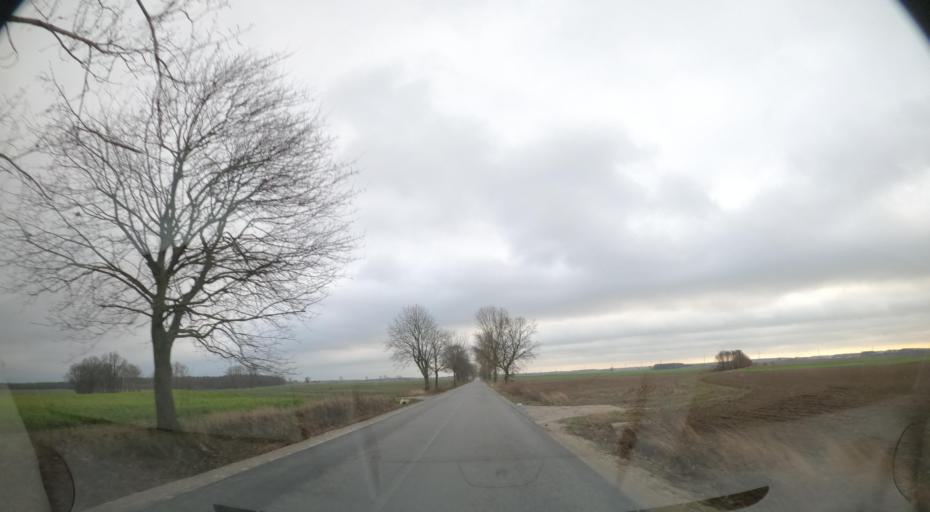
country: PL
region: Kujawsko-Pomorskie
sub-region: Powiat nakielski
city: Sadki
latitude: 53.2111
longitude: 17.3595
